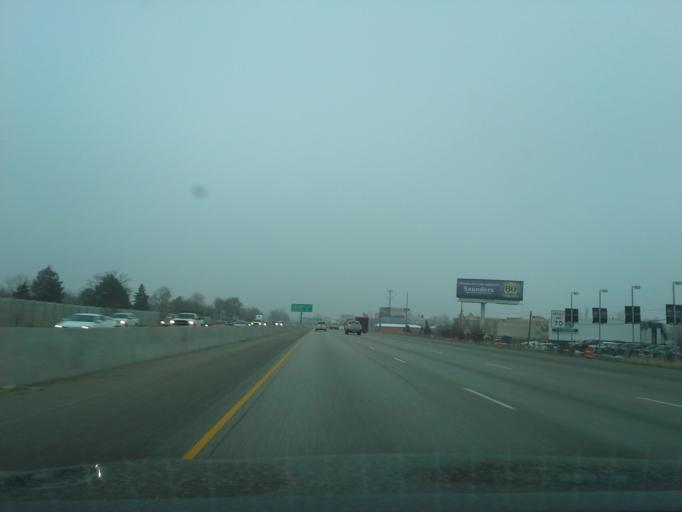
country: US
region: Utah
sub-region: Davis County
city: Layton
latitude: 41.0690
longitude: -111.9723
